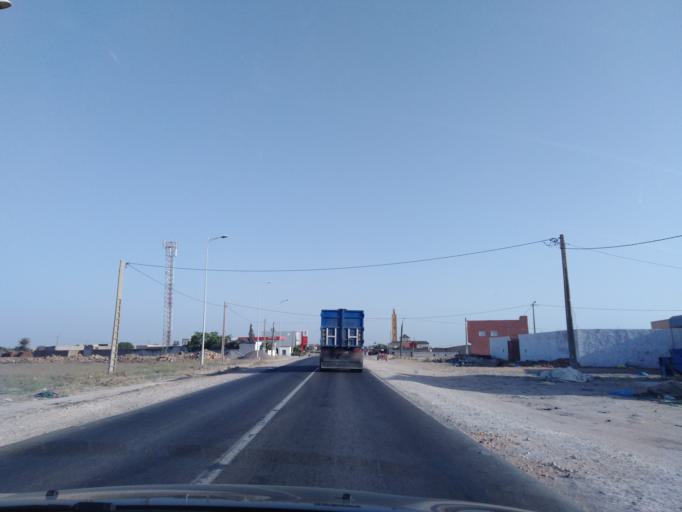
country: MA
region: Doukkala-Abda
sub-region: El-Jadida
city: Sidi Bennour
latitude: 32.5578
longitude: -8.7251
